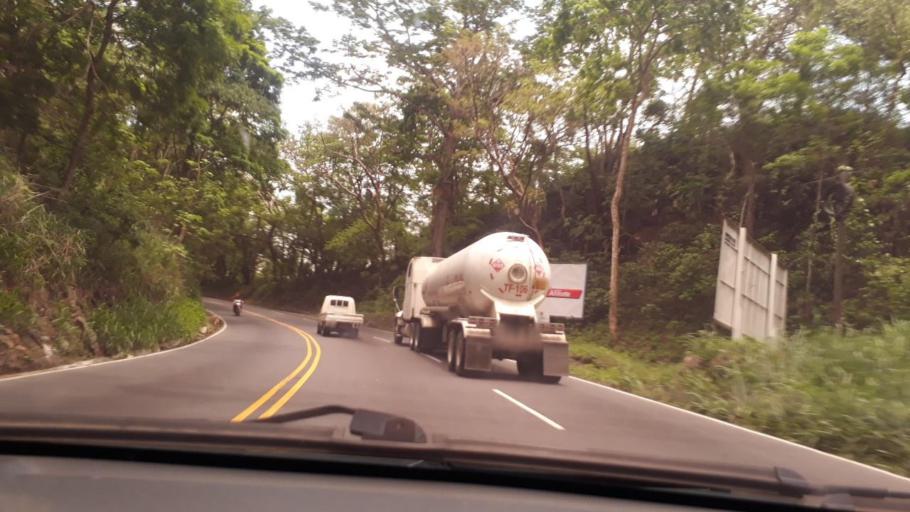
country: GT
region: Izabal
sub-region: Municipio de Los Amates
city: Los Amates
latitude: 15.2451
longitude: -89.1511
